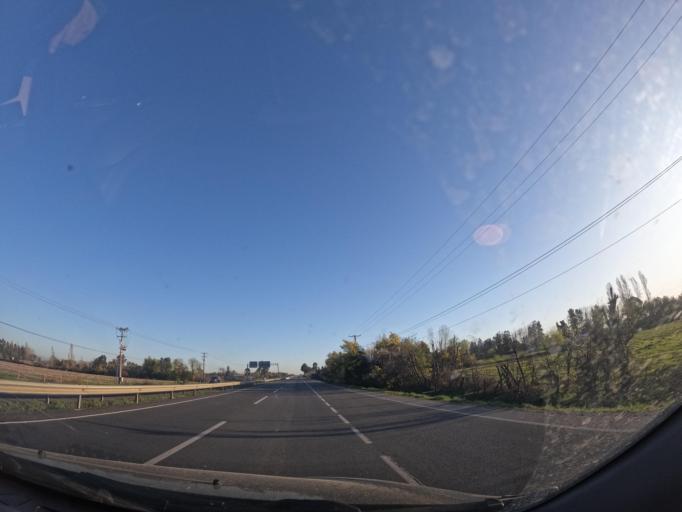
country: CL
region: Maule
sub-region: Provincia de Linares
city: Parral
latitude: -36.2879
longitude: -71.8219
